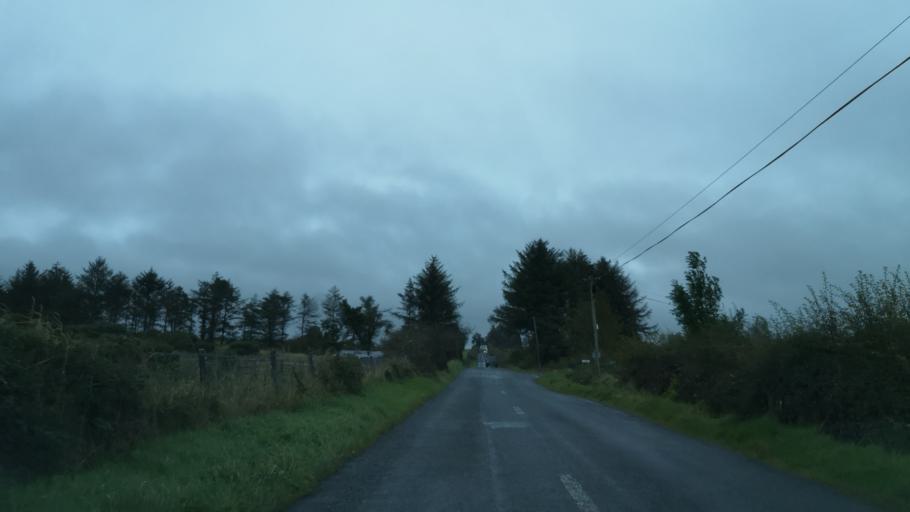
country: IE
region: Connaught
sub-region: Maigh Eo
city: Ballyhaunis
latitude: 53.7832
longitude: -8.7300
